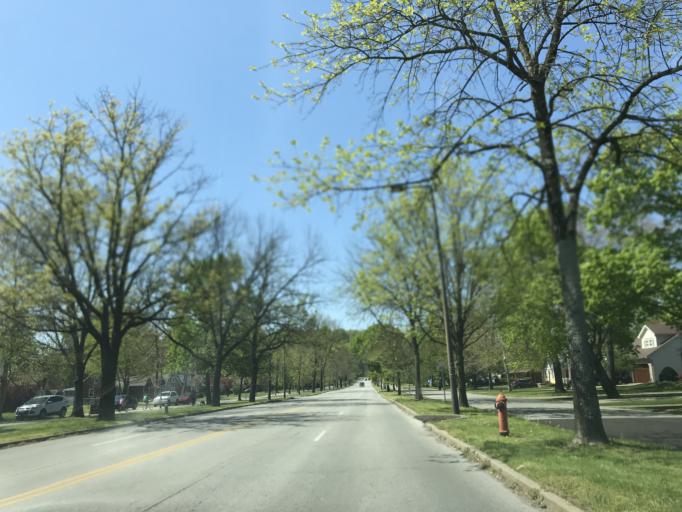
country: US
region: Kentucky
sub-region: Jefferson County
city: Shively
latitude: 38.1736
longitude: -85.7762
